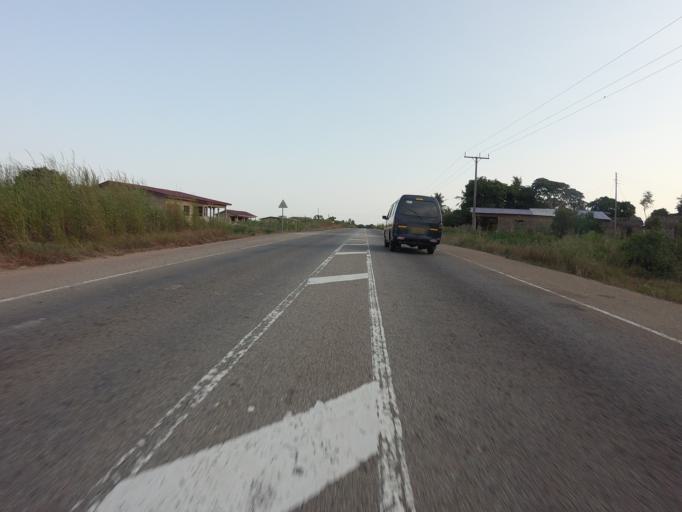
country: GH
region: Volta
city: Anloga
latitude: 6.0390
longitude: 0.6047
